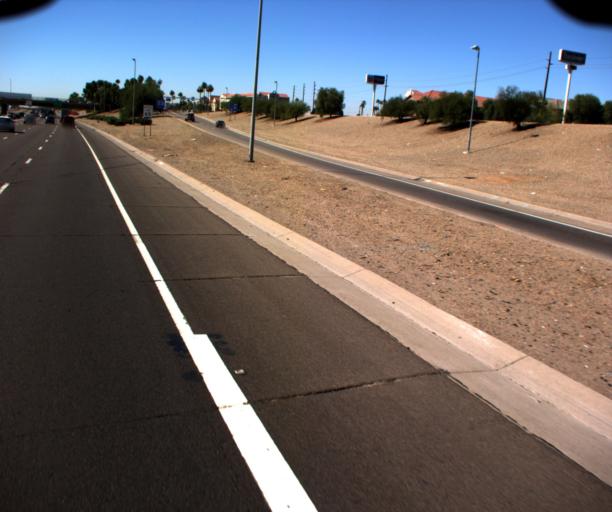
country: US
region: Arizona
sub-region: Maricopa County
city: Glendale
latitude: 33.4629
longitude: -112.1655
